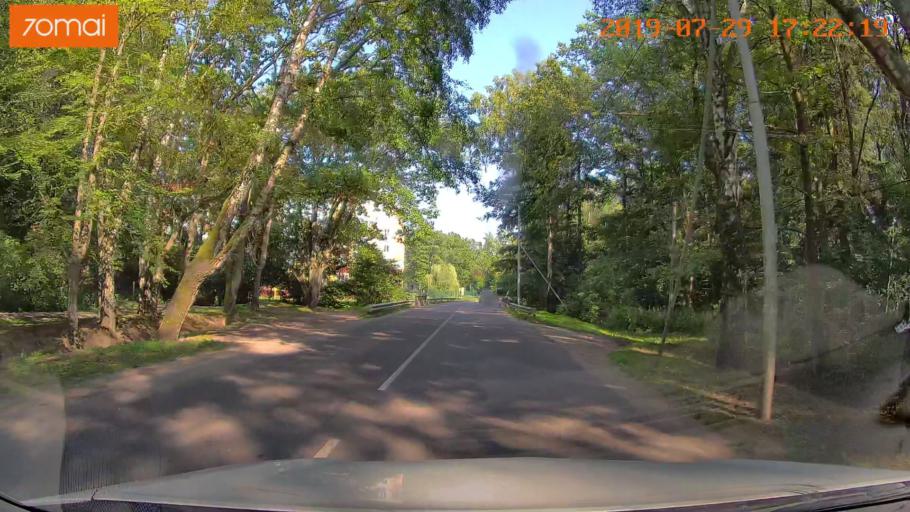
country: RU
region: Kaliningrad
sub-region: Gorod Kaliningrad
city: Kaliningrad
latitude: 54.7692
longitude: 20.4415
